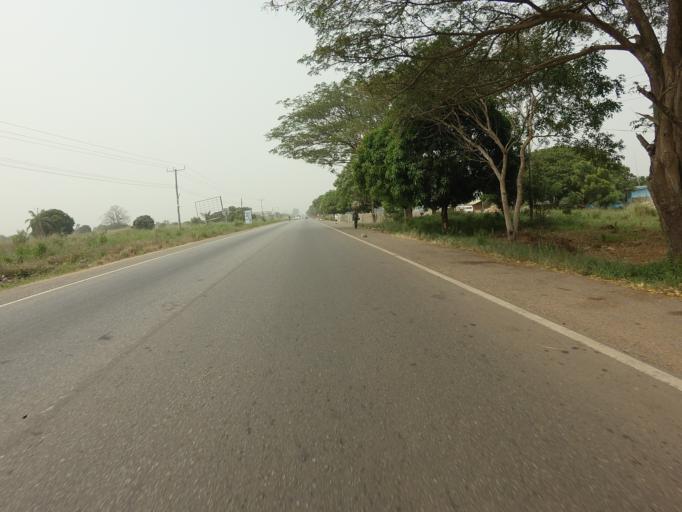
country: GH
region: Volta
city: Anloga
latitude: 5.8953
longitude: 0.5102
